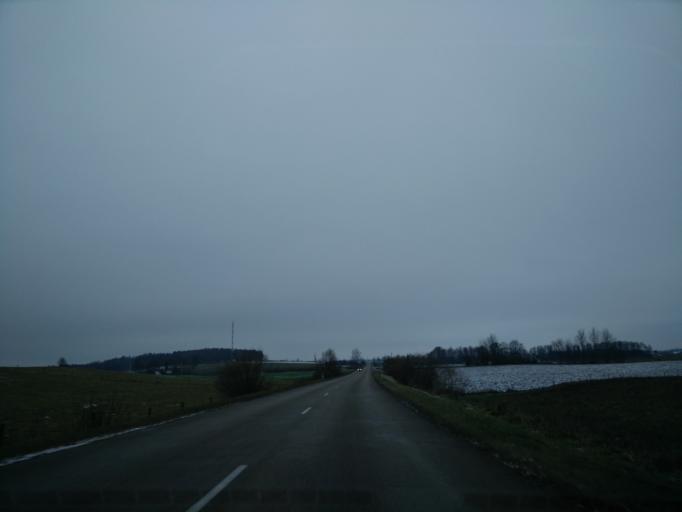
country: LT
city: Ariogala
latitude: 55.3396
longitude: 23.3975
